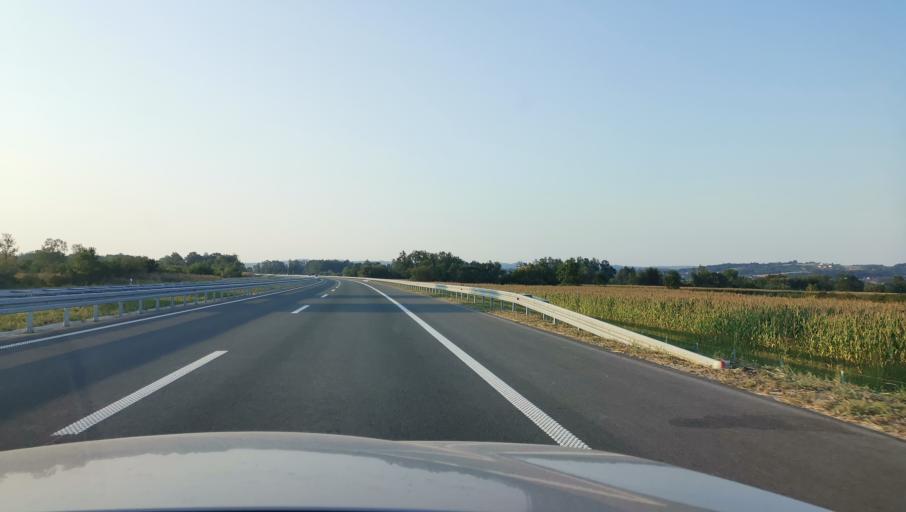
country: RS
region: Central Serbia
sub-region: Kolubarski Okrug
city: Ljig
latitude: 44.2613
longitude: 20.2711
